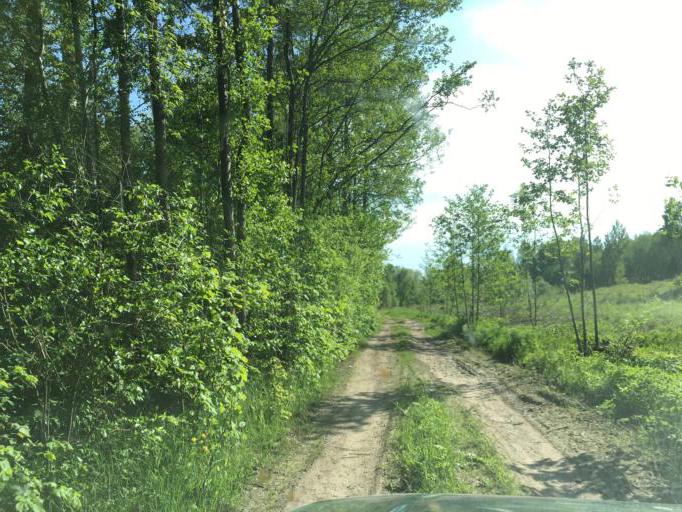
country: LV
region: Dundaga
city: Dundaga
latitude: 57.6029
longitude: 22.5082
